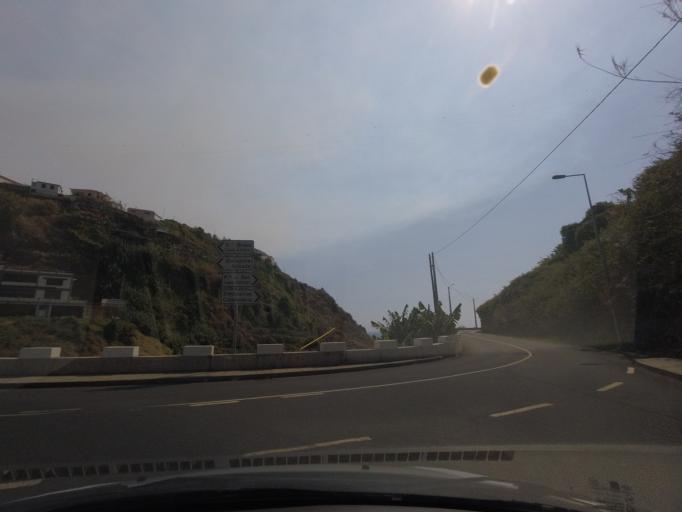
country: PT
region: Madeira
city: Ponta do Sol
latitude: 32.6837
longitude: -17.0750
